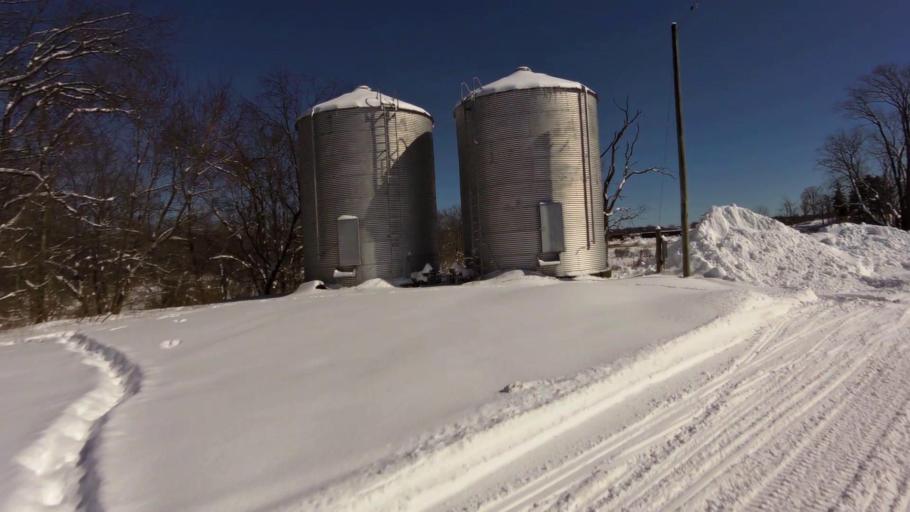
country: US
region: New York
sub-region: Chautauqua County
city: Mayville
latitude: 42.1650
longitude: -79.5840
